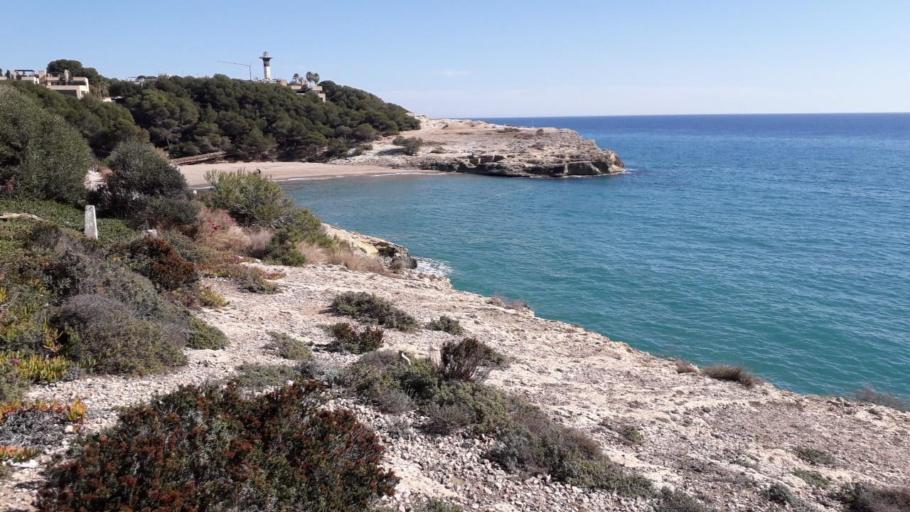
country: ES
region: Catalonia
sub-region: Provincia de Tarragona
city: Torredembarra
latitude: 41.1325
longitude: 1.3882
